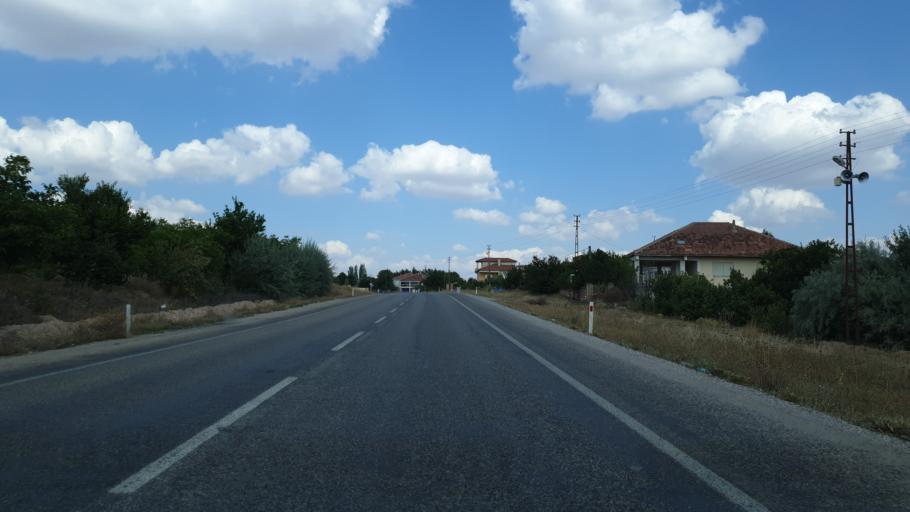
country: TR
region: Kayseri
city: Felahiye
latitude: 39.1053
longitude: 35.5963
